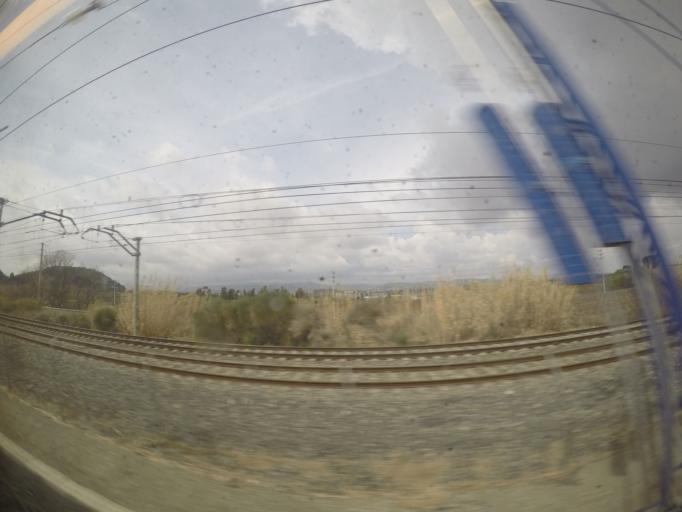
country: ES
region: Catalonia
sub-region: Provincia de Barcelona
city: Castellet
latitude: 41.2815
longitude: 1.6093
